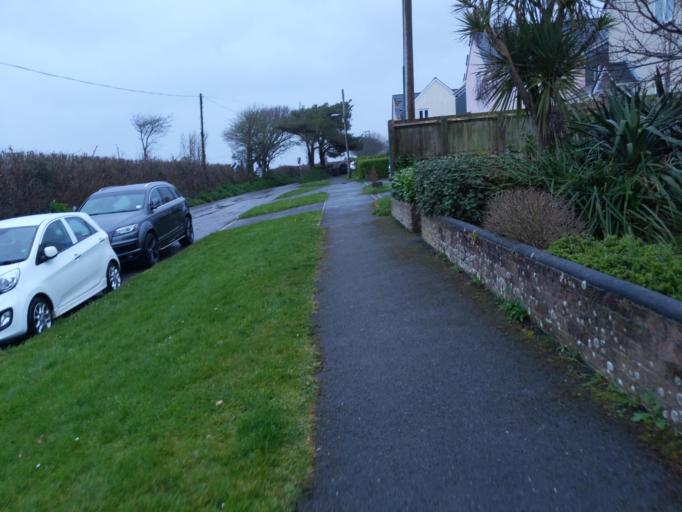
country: GB
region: England
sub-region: Devon
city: Yealmpton
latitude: 50.3232
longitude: -4.0314
